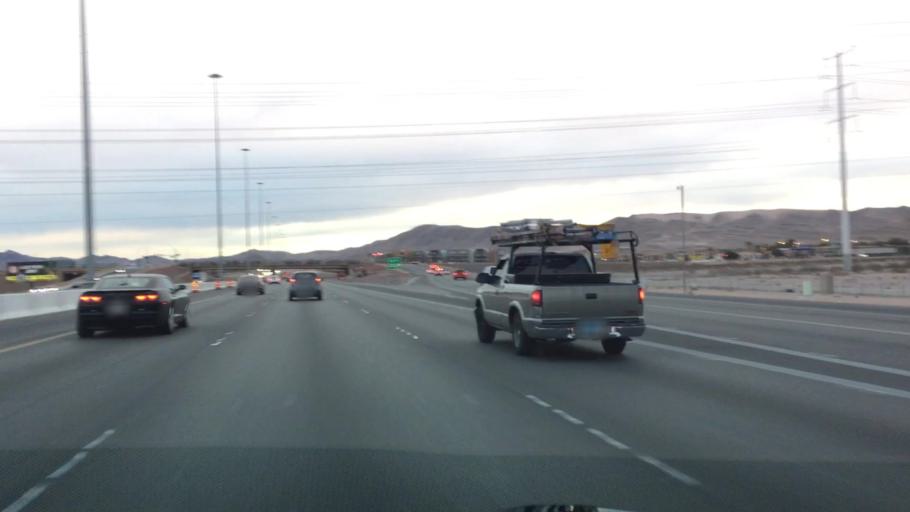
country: US
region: Nevada
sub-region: Clark County
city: Enterprise
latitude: 36.0036
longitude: -115.1807
